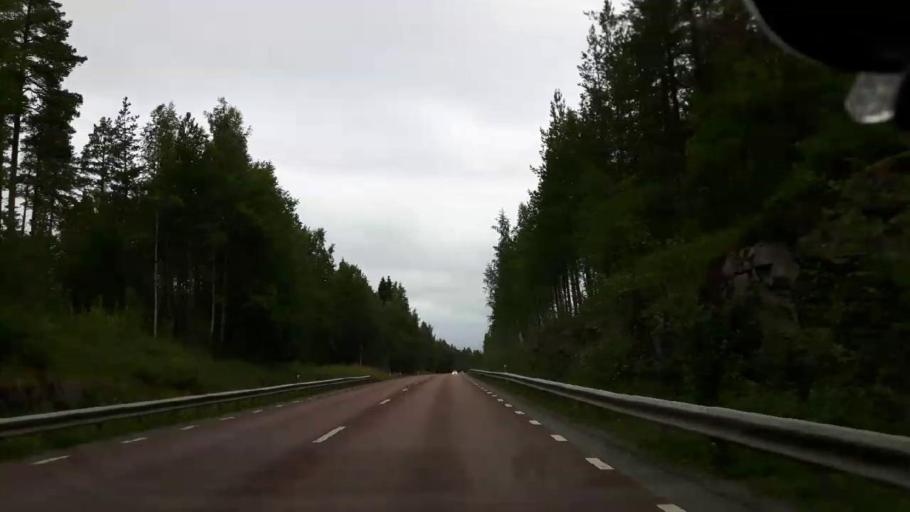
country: SE
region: Jaemtland
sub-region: Bergs Kommun
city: Hoverberg
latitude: 62.8785
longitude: 14.5224
